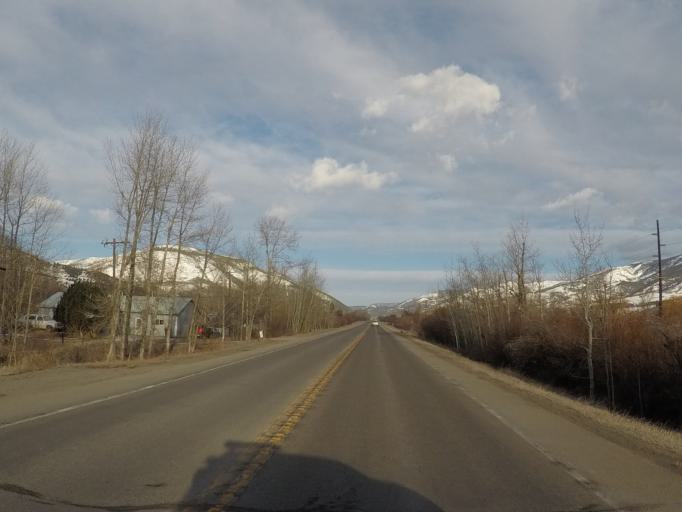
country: US
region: Montana
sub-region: Deer Lodge County
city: Anaconda
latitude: 46.1426
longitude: -112.9932
